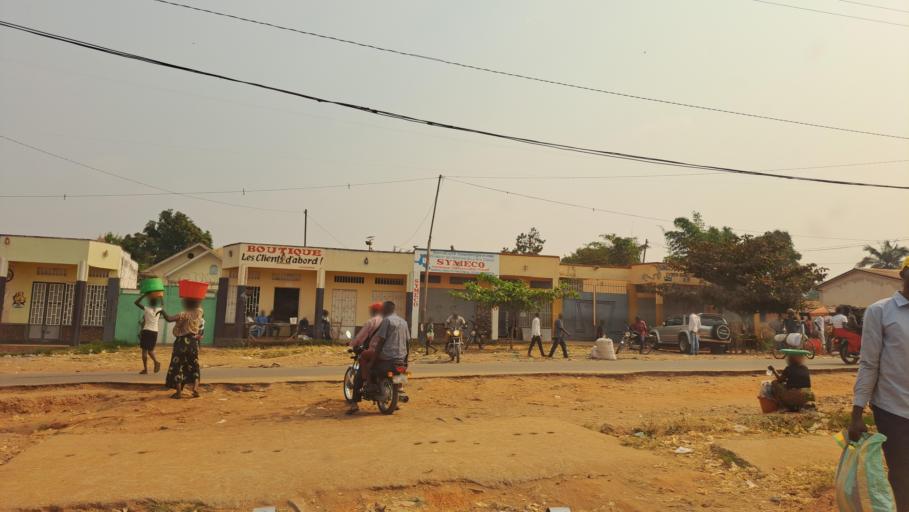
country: CD
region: Kasai-Oriental
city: Mbuji-Mayi
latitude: -6.1260
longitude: 23.5998
